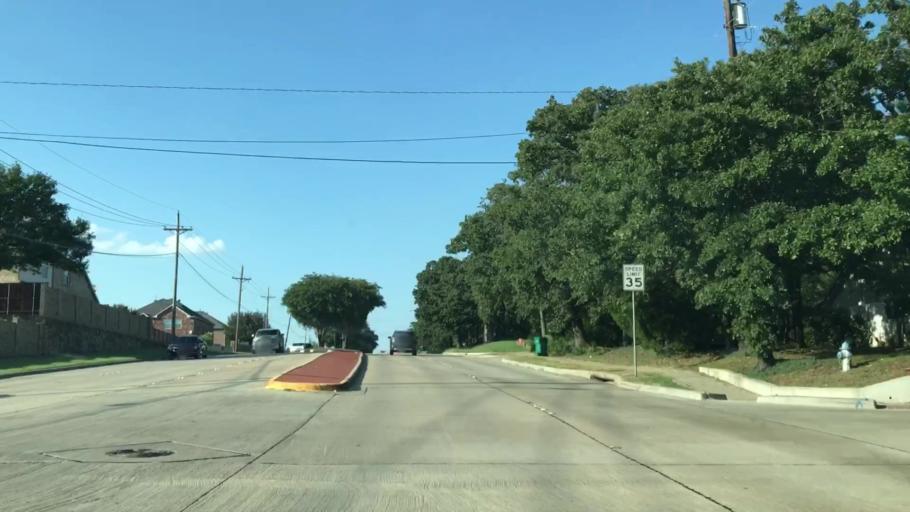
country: US
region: Texas
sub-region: Denton County
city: Lewisville
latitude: 33.0245
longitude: -97.0191
